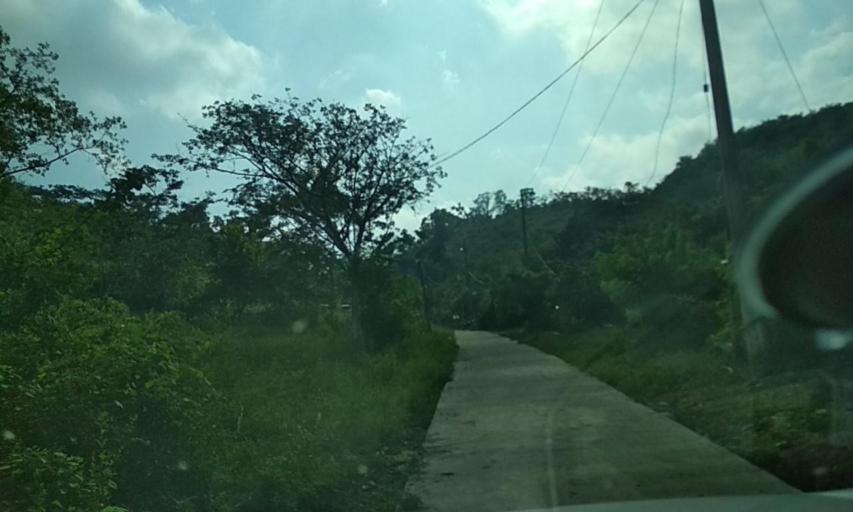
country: MX
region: Veracruz
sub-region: Cazones de Herrera
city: Rancho Nuevo
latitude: 20.6194
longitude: -97.2205
